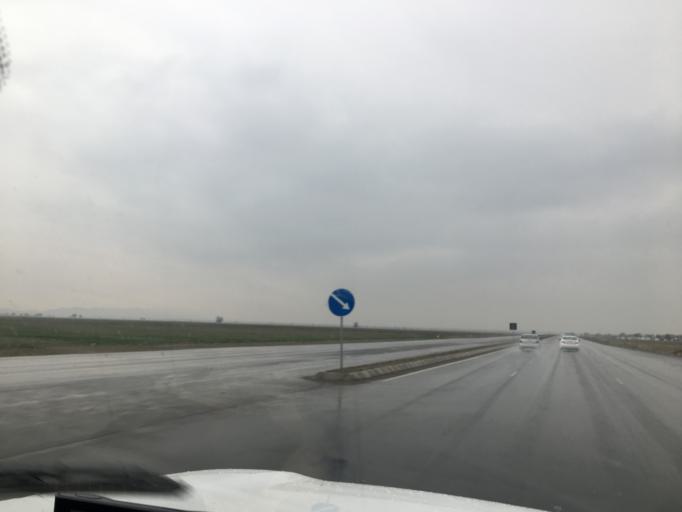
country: TM
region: Ahal
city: Annau
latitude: 37.8208
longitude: 58.7647
